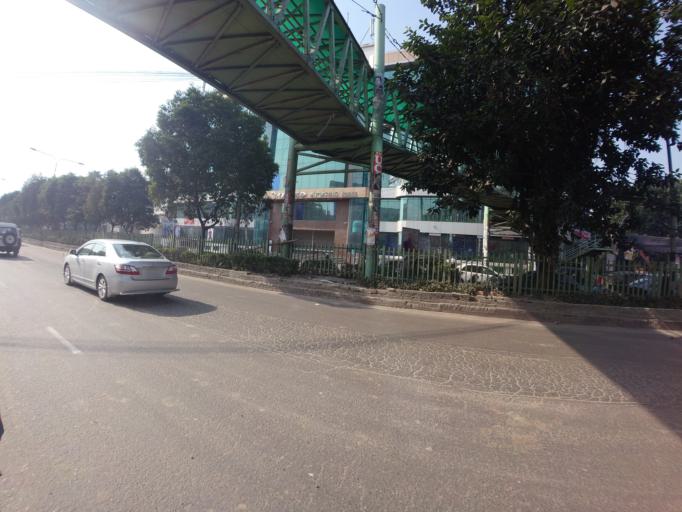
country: BD
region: Dhaka
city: Azimpur
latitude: 23.7527
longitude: 90.3775
